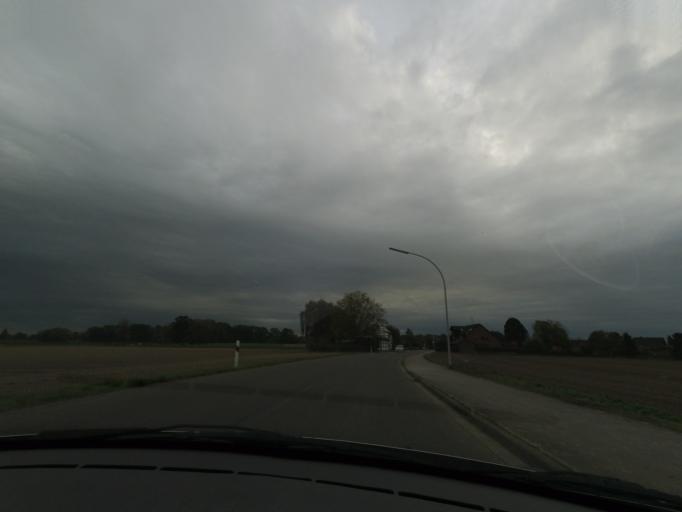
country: DE
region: North Rhine-Westphalia
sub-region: Regierungsbezirk Dusseldorf
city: Korschenbroich
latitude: 51.1743
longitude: 6.5459
